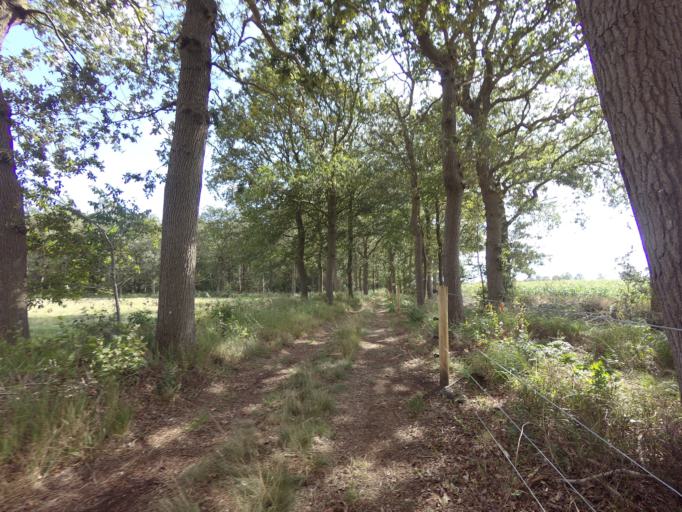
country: NL
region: Friesland
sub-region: Gemeente Weststellingwerf
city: Noordwolde
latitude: 52.9513
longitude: 6.1891
